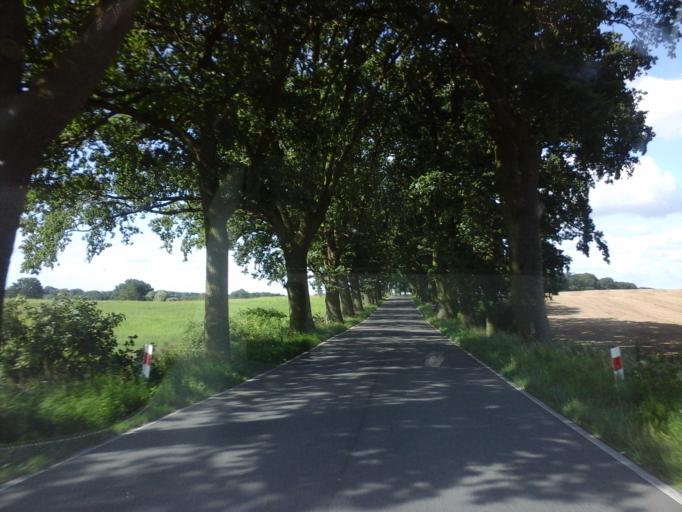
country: PL
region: West Pomeranian Voivodeship
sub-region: Powiat stargardzki
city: Dolice
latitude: 53.1980
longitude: 15.2404
